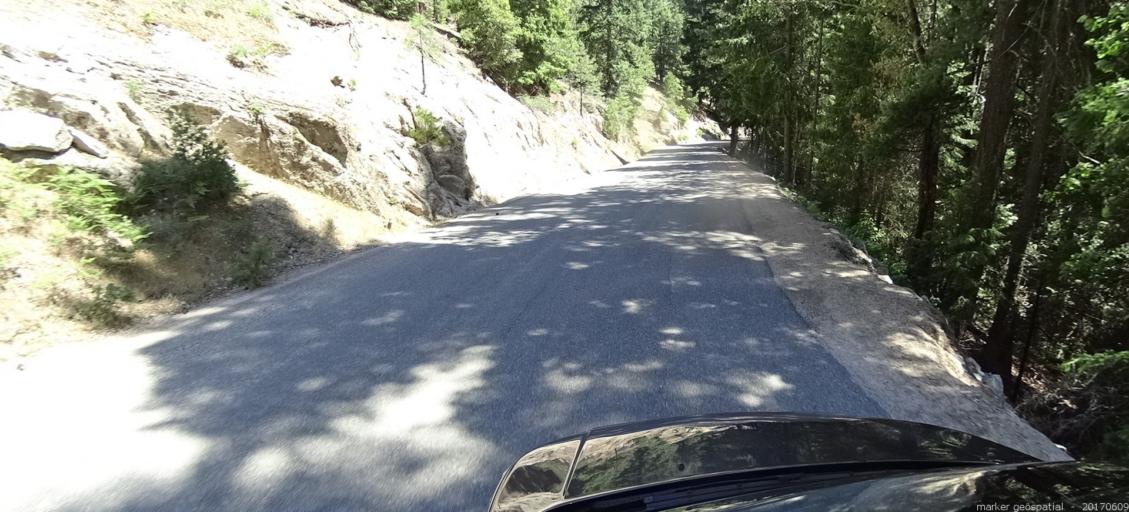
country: US
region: California
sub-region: Siskiyou County
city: Yreka
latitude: 41.4290
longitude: -122.9331
